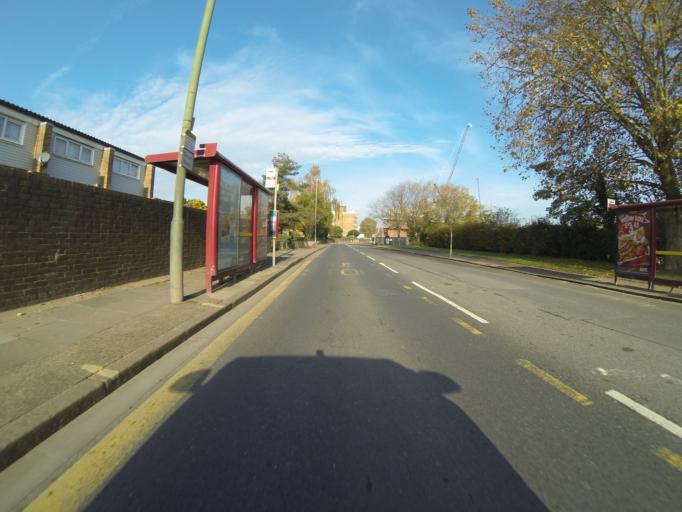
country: GB
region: England
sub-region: Kent
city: Dartford
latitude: 51.4392
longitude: 0.2154
